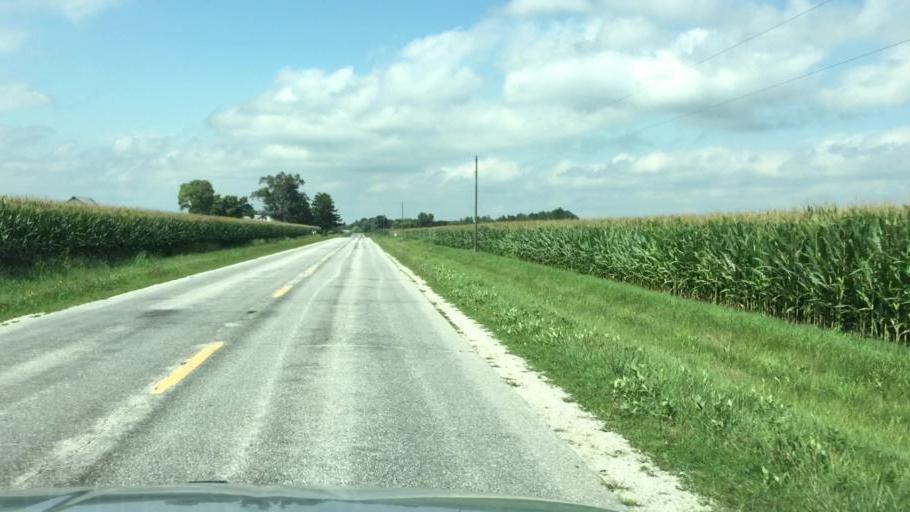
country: US
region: Illinois
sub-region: Hancock County
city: Nauvoo
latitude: 40.5150
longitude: -91.3080
